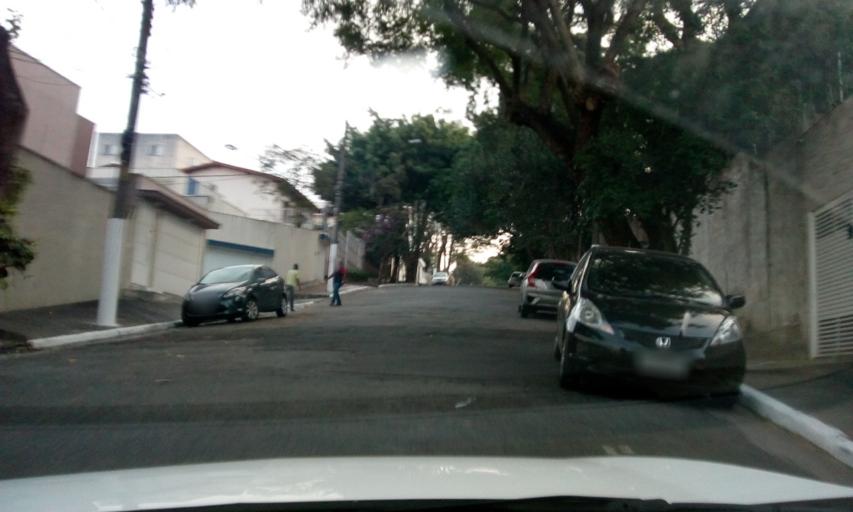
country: BR
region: Sao Paulo
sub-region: Diadema
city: Diadema
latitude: -23.6212
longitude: -46.6433
